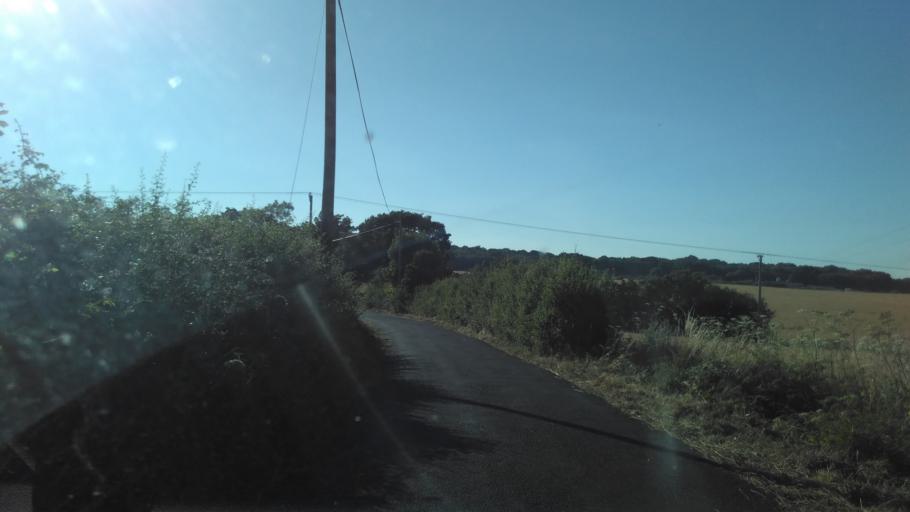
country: GB
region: England
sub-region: Kent
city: Blean
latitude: 51.3159
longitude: 1.0302
